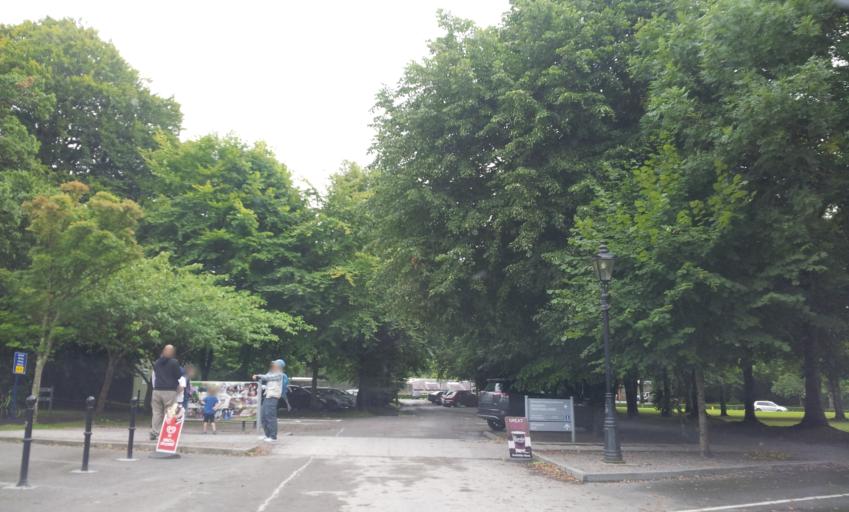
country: IE
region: Munster
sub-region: Ciarrai
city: Cill Airne
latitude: 52.0198
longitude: -9.5006
